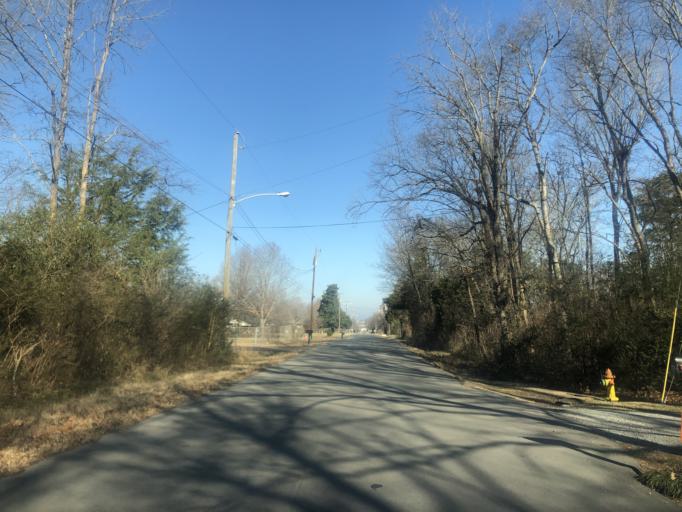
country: US
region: Tennessee
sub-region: Rutherford County
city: La Vergne
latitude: 36.0084
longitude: -86.5851
